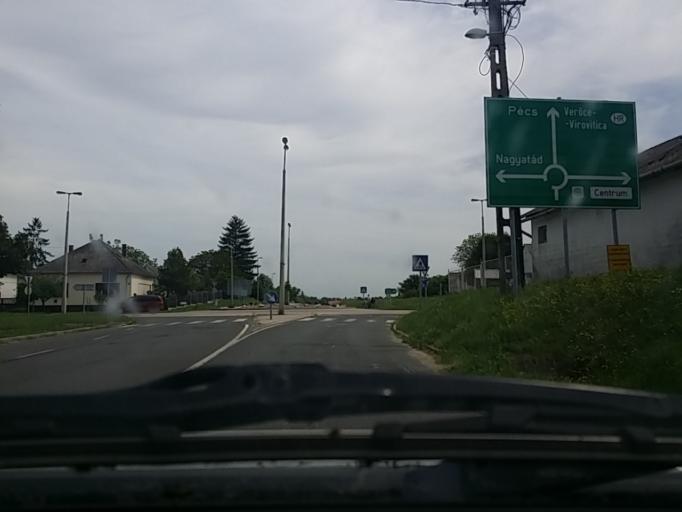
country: HU
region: Somogy
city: Barcs
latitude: 45.9660
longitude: 17.4583
